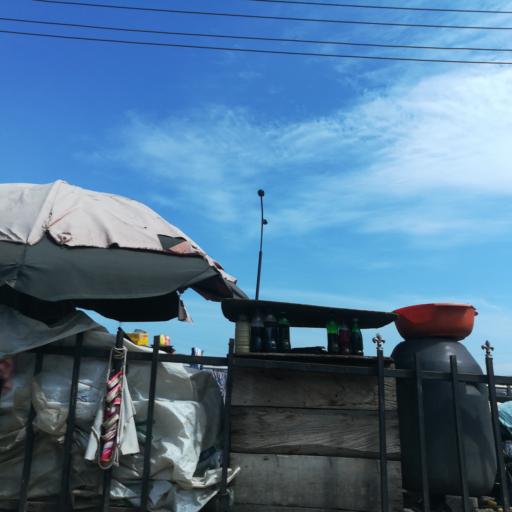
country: NG
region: Lagos
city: Lagos
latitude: 6.4652
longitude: 3.3884
